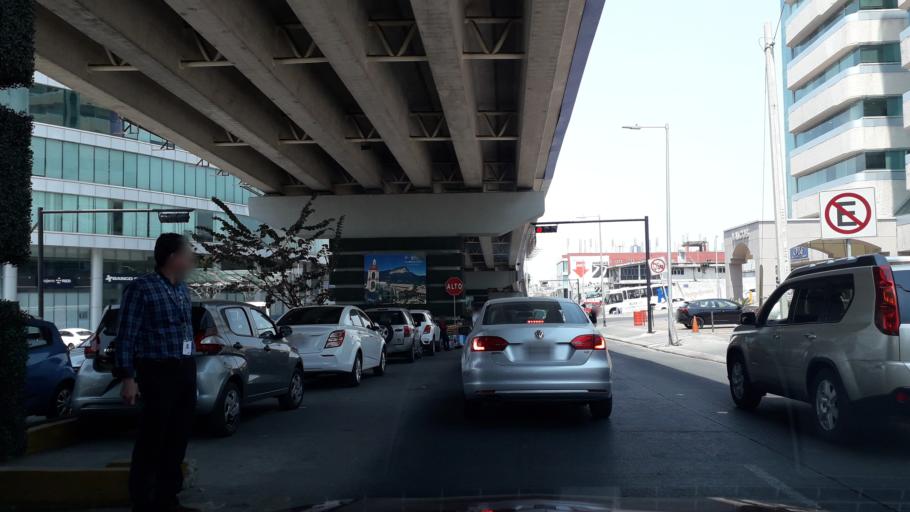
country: MX
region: Puebla
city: Puebla
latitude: 19.0482
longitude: -98.2364
